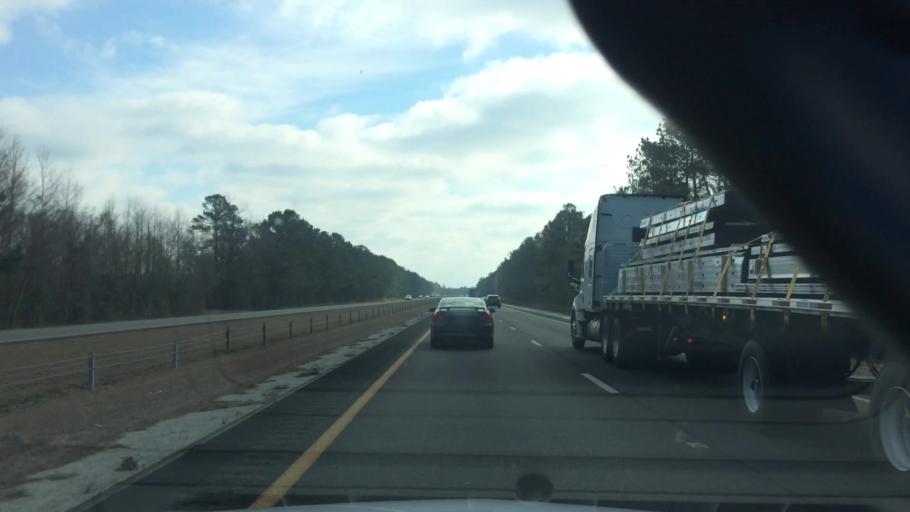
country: US
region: North Carolina
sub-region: Pender County
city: Burgaw
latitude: 34.6007
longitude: -77.9131
